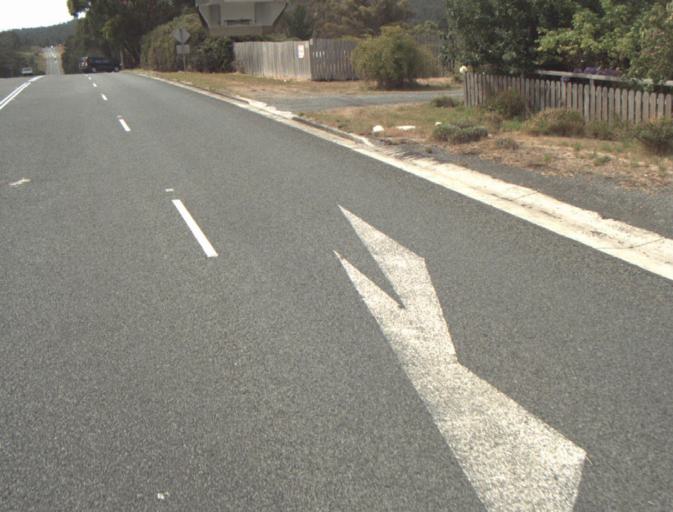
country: AU
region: Tasmania
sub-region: Launceston
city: Mayfield
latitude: -41.2784
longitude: 147.0378
